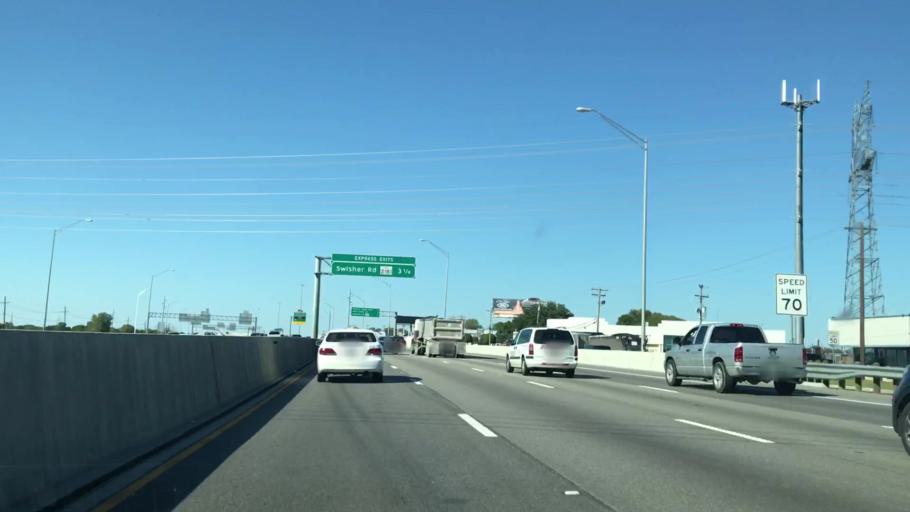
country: US
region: Texas
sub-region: Denton County
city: Lewisville
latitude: 33.0642
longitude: -97.0146
